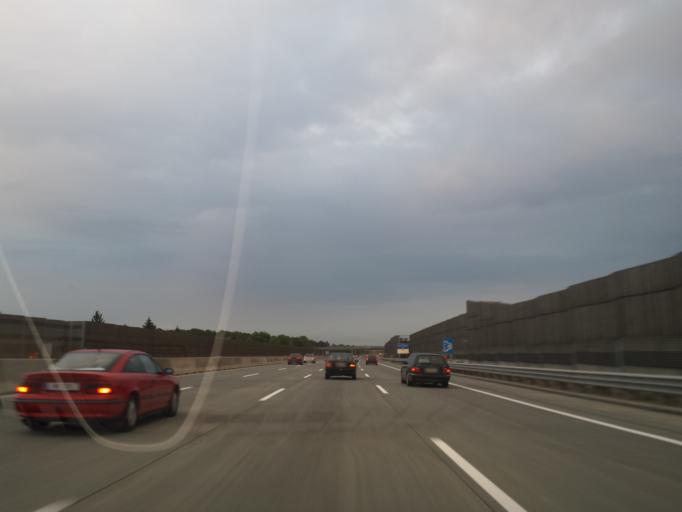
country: AT
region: Lower Austria
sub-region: Politischer Bezirk Baden
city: Kottingbrunn
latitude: 47.9636
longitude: 16.2289
